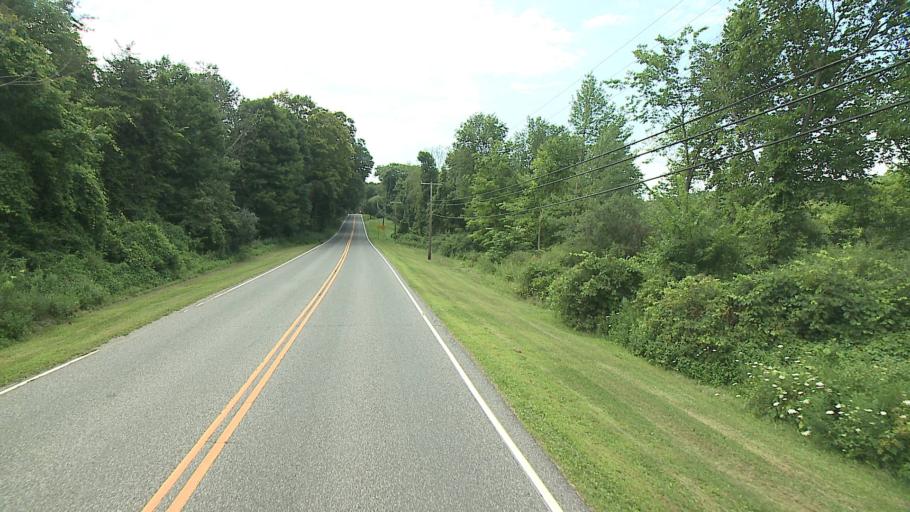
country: US
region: Connecticut
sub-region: Fairfield County
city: Sherman
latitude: 41.5853
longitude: -73.4987
